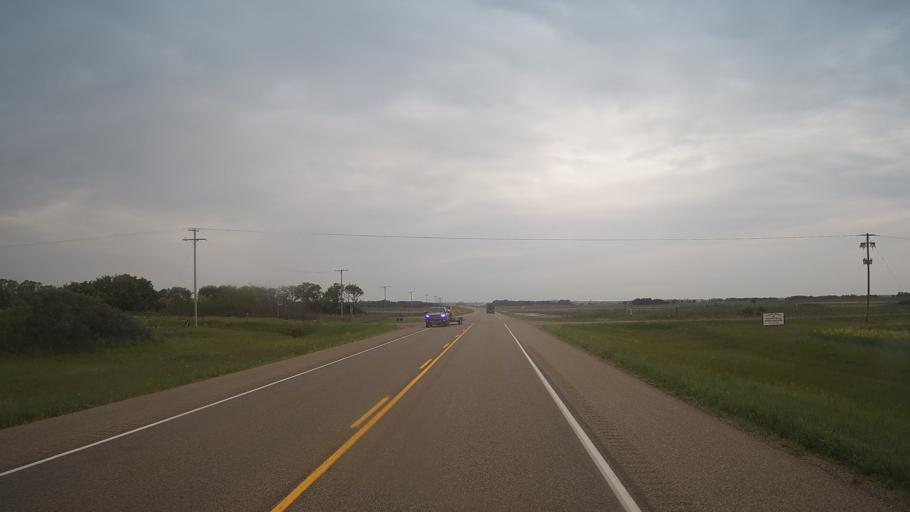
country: CA
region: Saskatchewan
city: Langham
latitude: 52.1294
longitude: -107.0971
